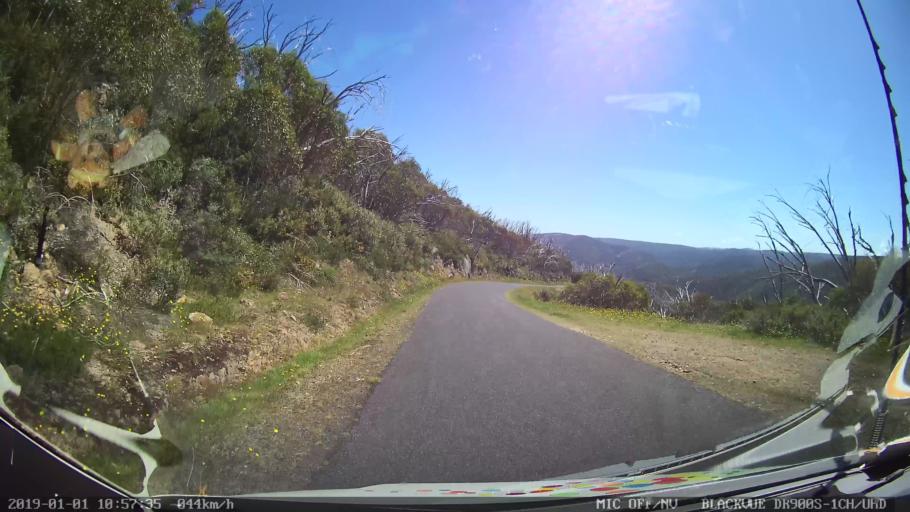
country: AU
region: New South Wales
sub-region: Snowy River
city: Jindabyne
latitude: -35.9969
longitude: 148.3967
